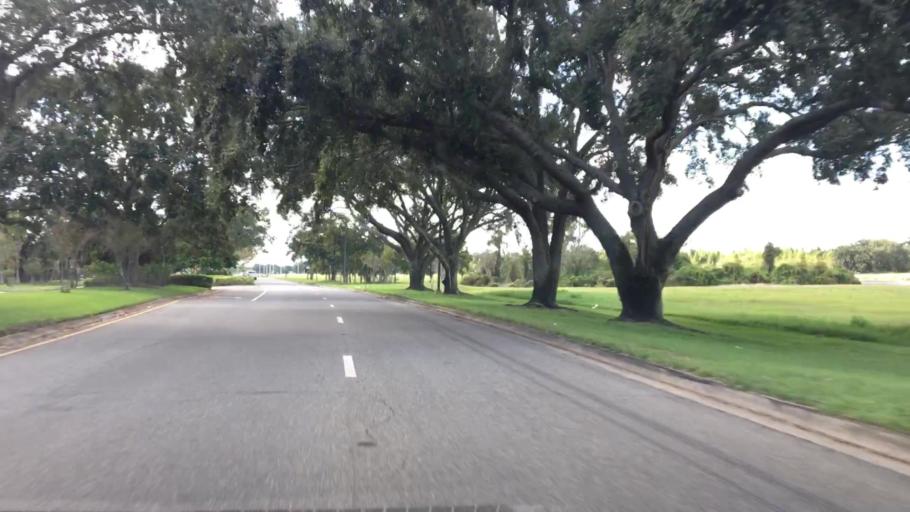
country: US
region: Florida
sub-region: Orange County
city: Conway
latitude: 28.4689
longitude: -81.3141
